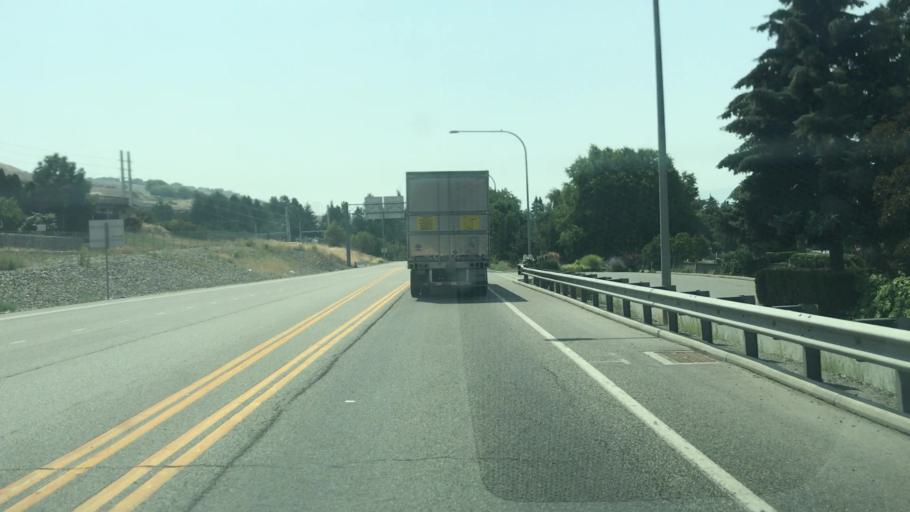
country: US
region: Washington
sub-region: Chelan County
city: Sunnyslope
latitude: 47.4660
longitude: -120.2988
